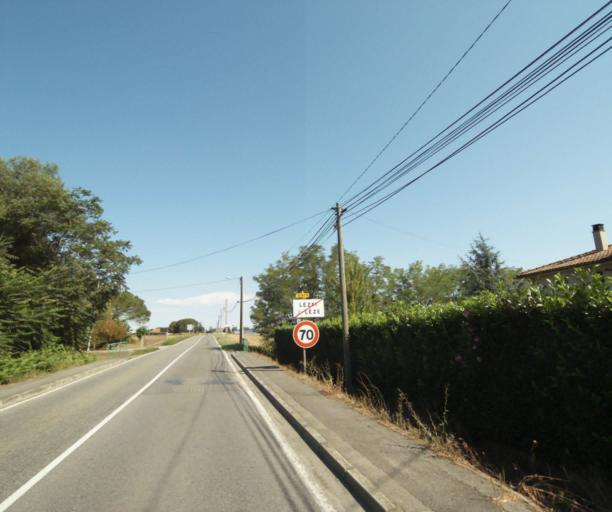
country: FR
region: Midi-Pyrenees
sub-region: Departement de l'Ariege
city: Lezat-sur-Leze
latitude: 43.2834
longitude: 1.3468
